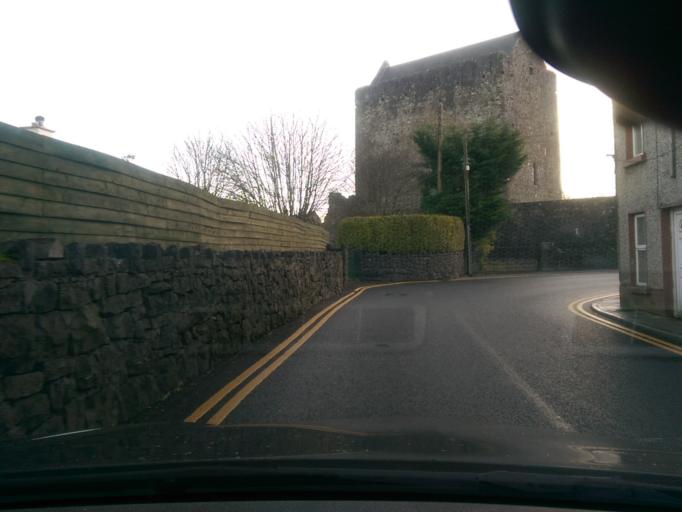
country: IE
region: Connaught
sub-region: County Galway
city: Athenry
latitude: 53.3003
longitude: -8.7453
